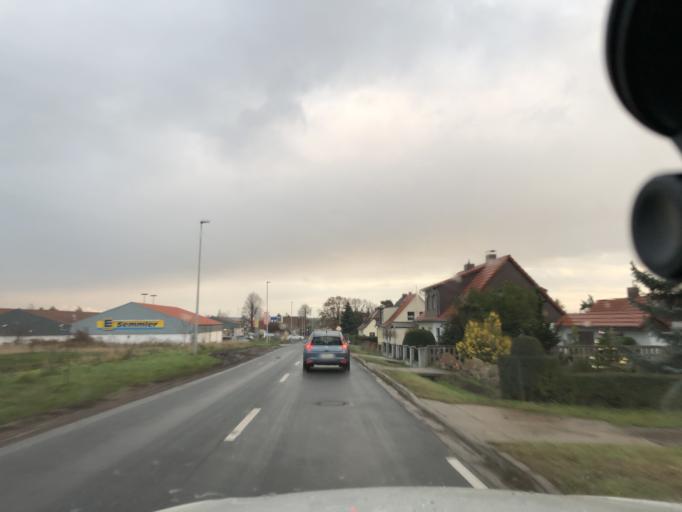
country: DE
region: Saxony-Anhalt
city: Teutschenthal
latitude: 51.4517
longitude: 11.7953
